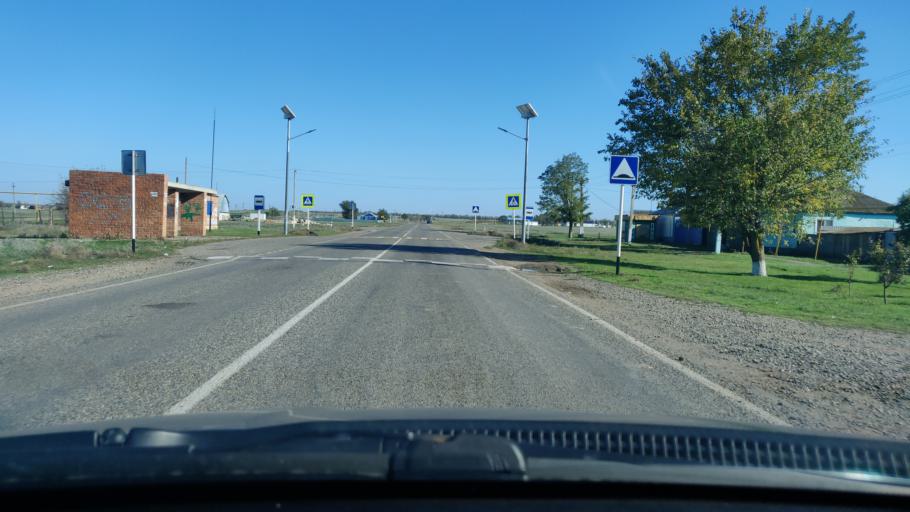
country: RU
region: Stavropol'skiy
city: Letnyaya Stavka
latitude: 45.3748
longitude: 43.6853
